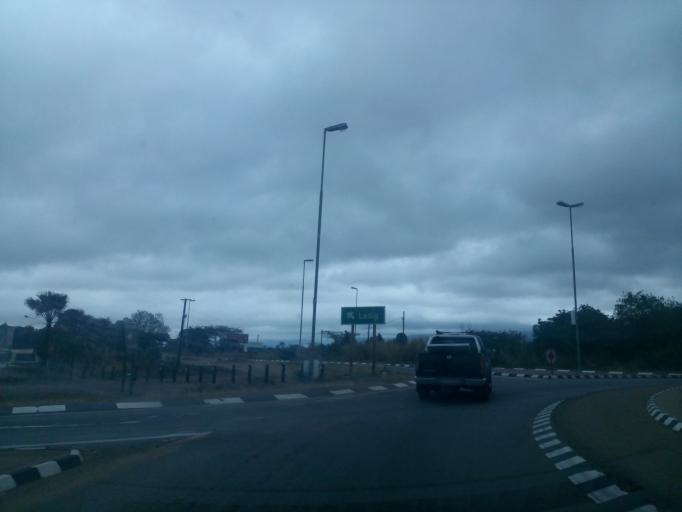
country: ZA
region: Limpopo
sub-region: Vhembe District Municipality
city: Louis Trichardt
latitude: -23.0785
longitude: 29.9087
